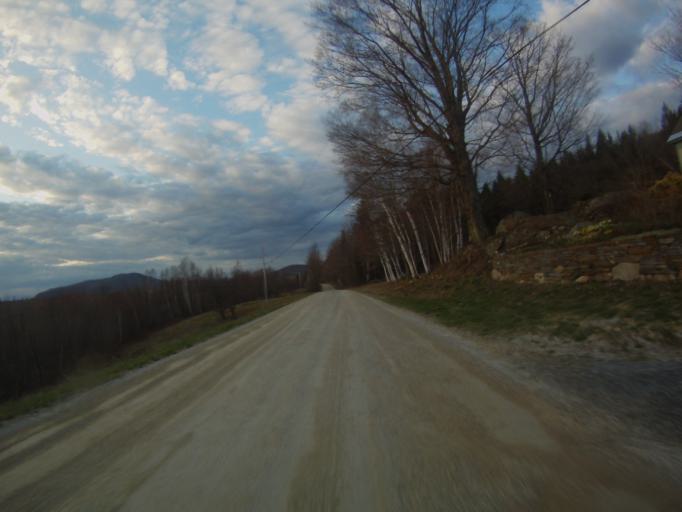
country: US
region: Vermont
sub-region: Rutland County
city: Brandon
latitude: 43.8780
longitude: -73.0126
